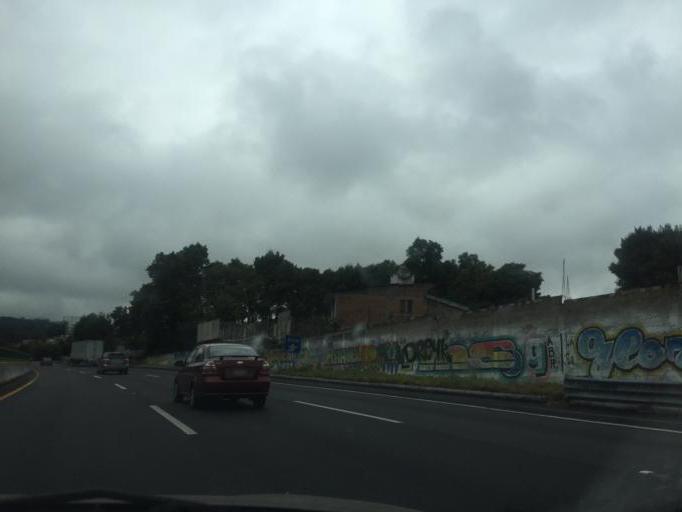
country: MX
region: Mexico City
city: Xochimilco
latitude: 19.2051
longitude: -99.1369
